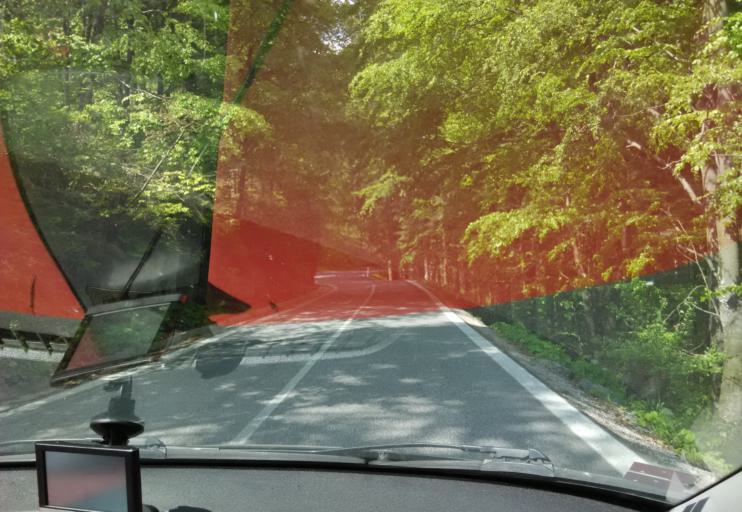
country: SK
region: Kosicky
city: Dobsina
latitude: 48.8483
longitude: 20.4487
